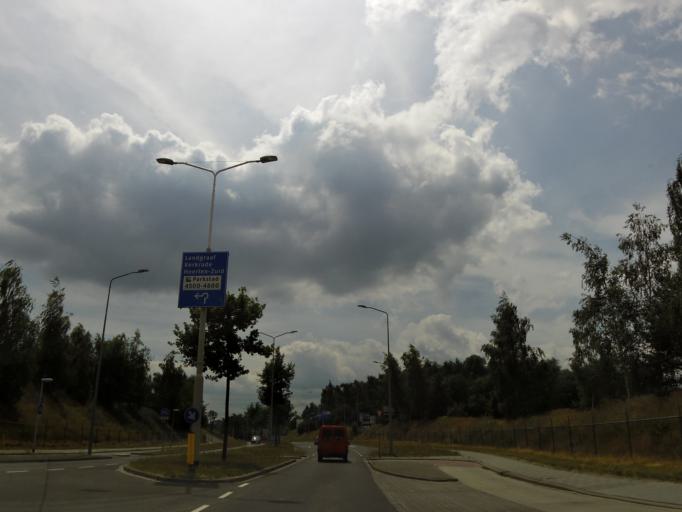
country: NL
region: Limburg
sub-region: Gemeente Heerlen
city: Heerlen
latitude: 50.9060
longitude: 5.9712
